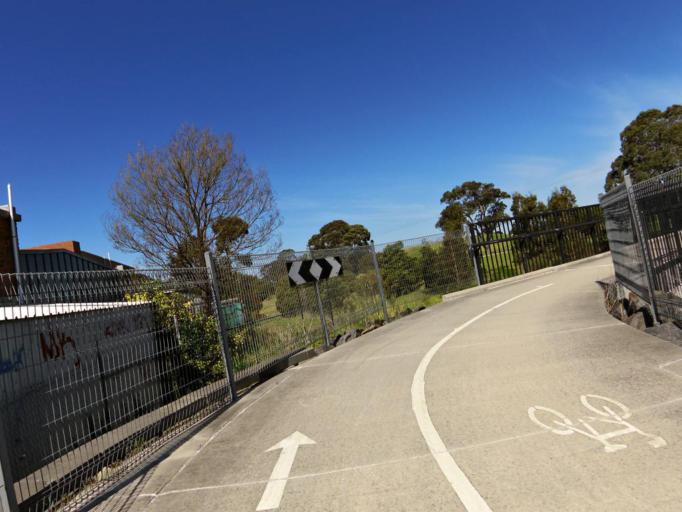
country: AU
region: Victoria
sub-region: Greater Dandenong
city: Dandenong
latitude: -37.9956
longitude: 145.1927
